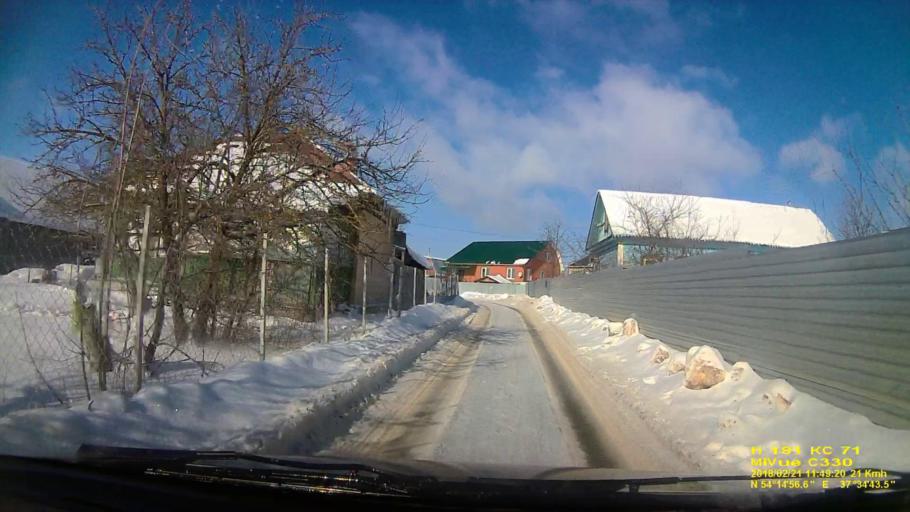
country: RU
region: Tula
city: Gorelki
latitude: 54.2492
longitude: 37.5796
